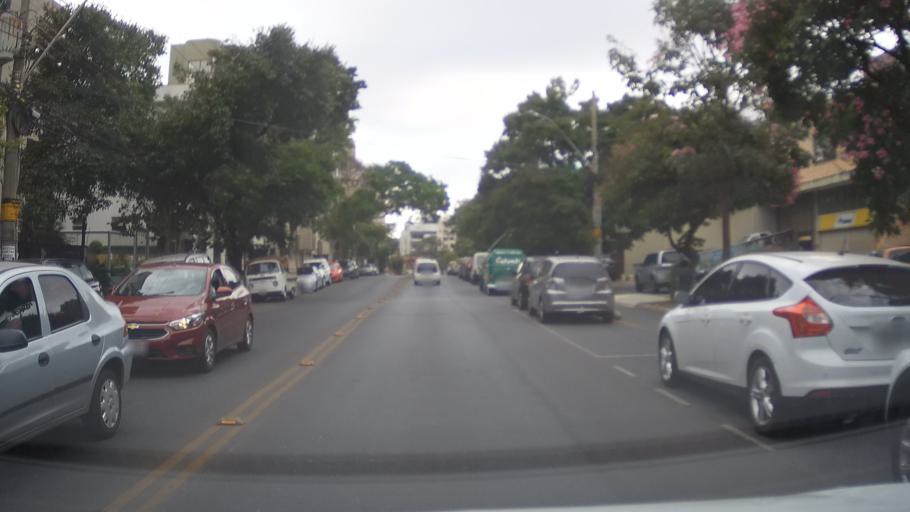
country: BR
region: Minas Gerais
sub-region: Belo Horizonte
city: Belo Horizonte
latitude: -19.9535
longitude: -43.9253
